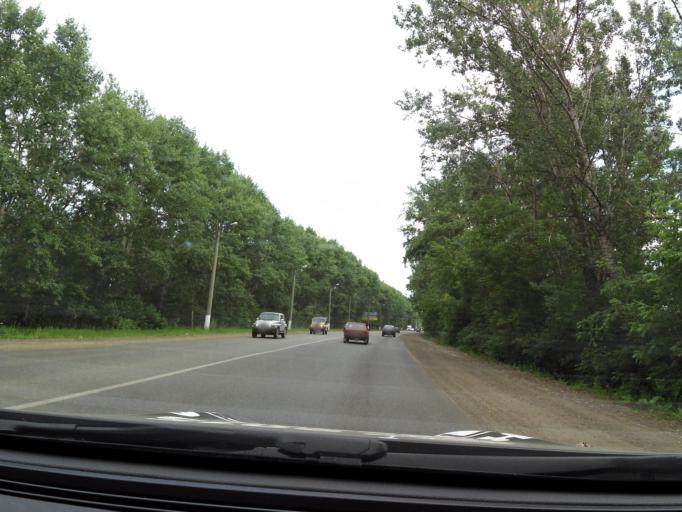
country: RU
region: Kirov
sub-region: Kirovo-Chepetskiy Rayon
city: Kirov
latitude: 58.6184
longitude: 49.7321
